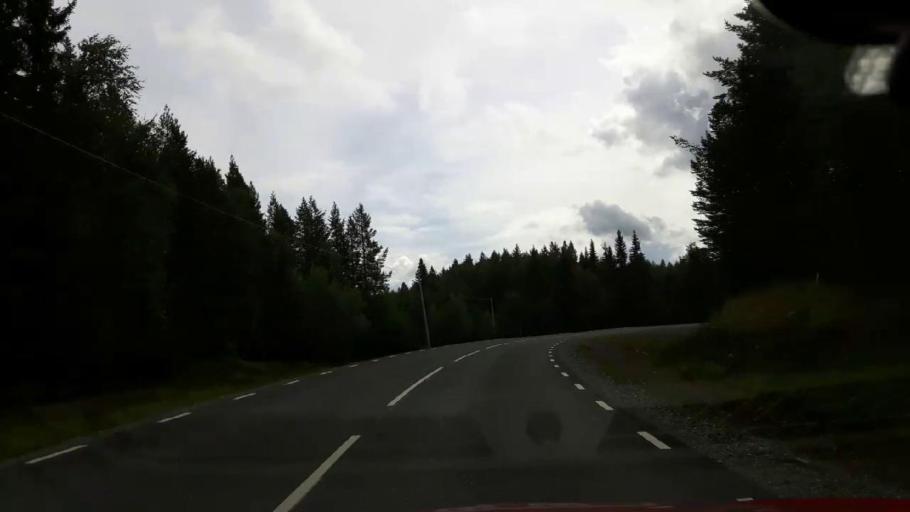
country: NO
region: Nord-Trondelag
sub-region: Lierne
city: Sandvika
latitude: 64.5873
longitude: 14.1223
